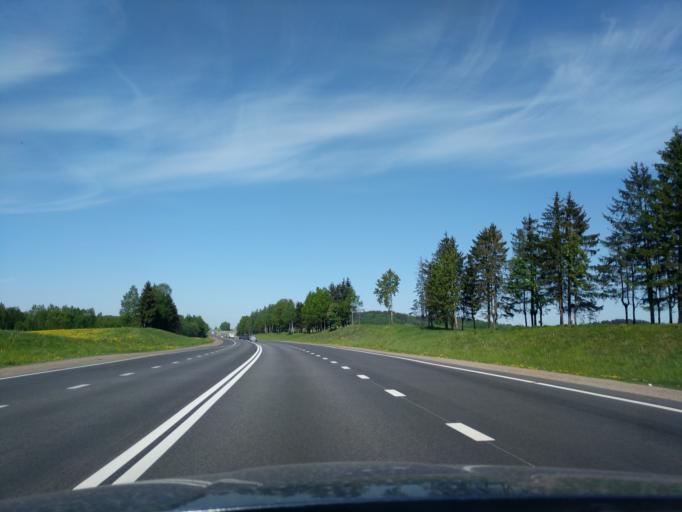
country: BY
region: Minsk
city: Bal'shavik
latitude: 54.0864
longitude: 27.5497
